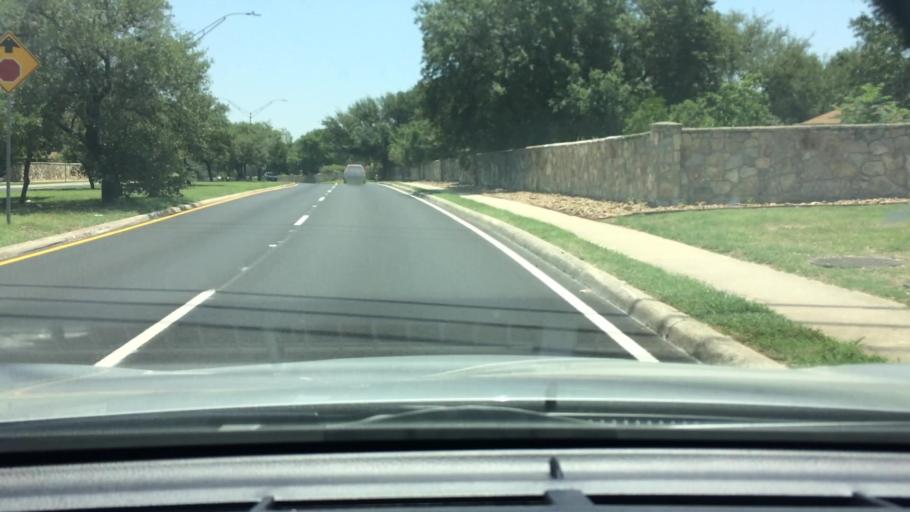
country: US
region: Texas
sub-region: Bexar County
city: Shavano Park
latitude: 29.5589
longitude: -98.5800
